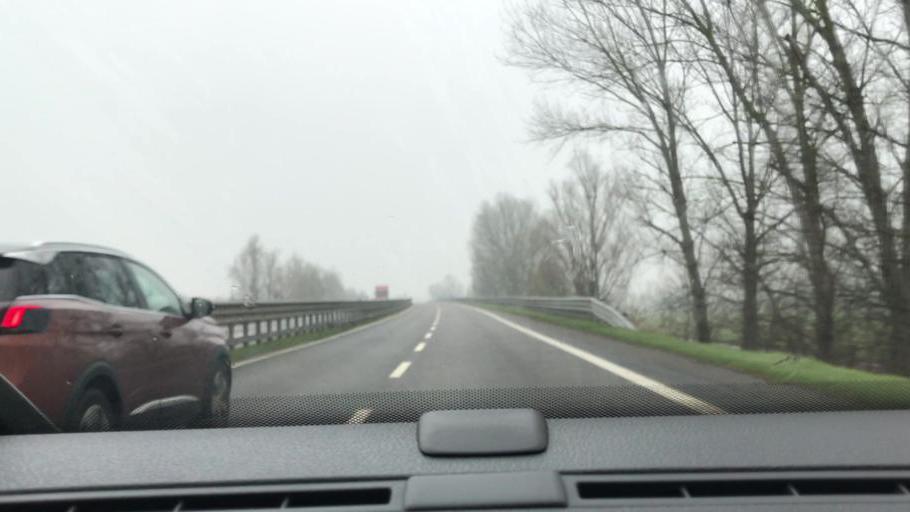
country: IT
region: Veneto
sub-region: Provincia di Rovigo
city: Badia Polesine
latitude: 45.0756
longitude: 11.4781
